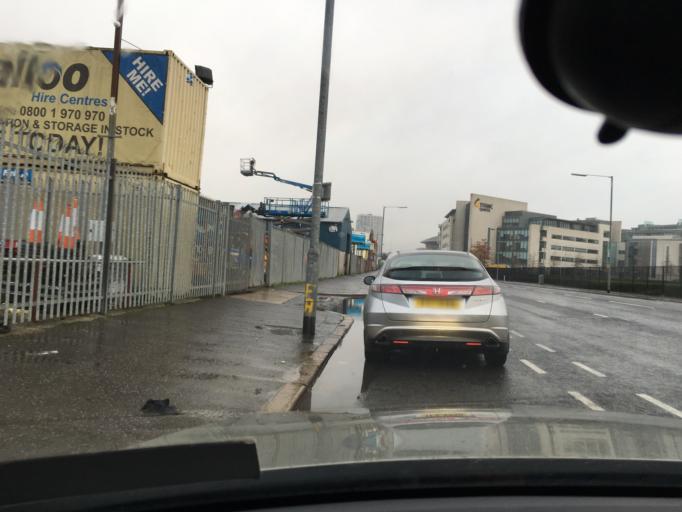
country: GB
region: Northern Ireland
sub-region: City of Belfast
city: Belfast
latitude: 54.6032
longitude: -5.9074
